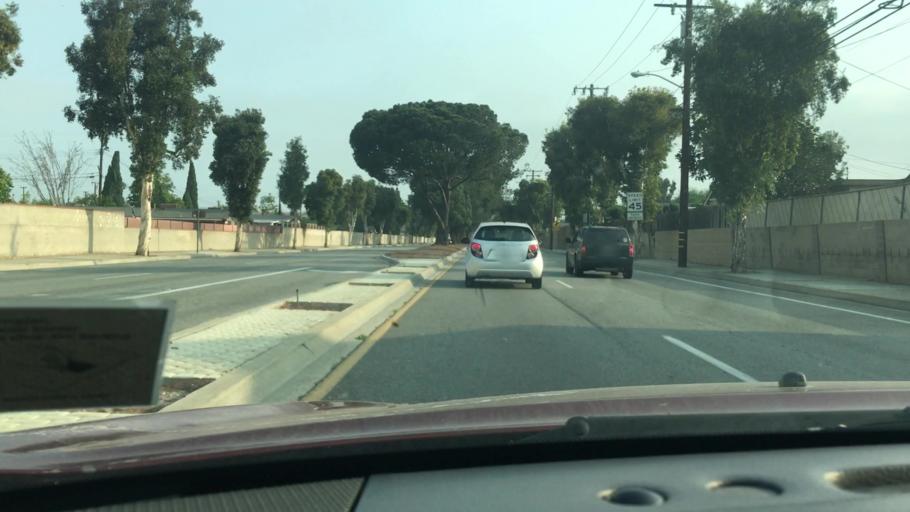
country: US
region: California
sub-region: Los Angeles County
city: La Mirada
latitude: 33.9102
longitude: -118.0292
